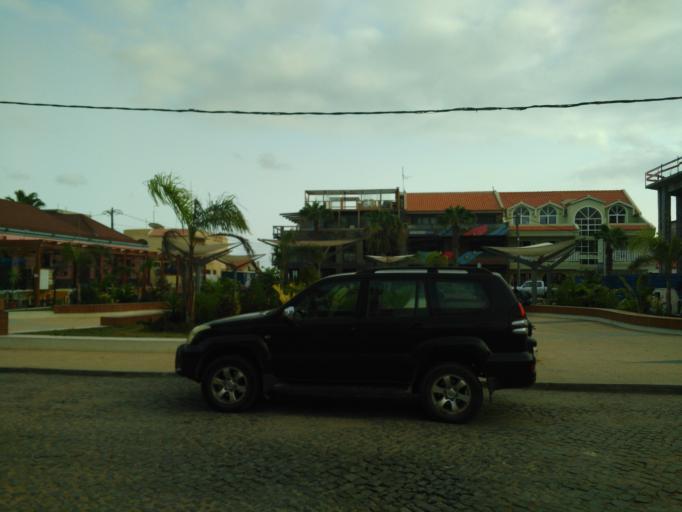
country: CV
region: Sal
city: Santa Maria
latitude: 16.5986
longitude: -22.9056
